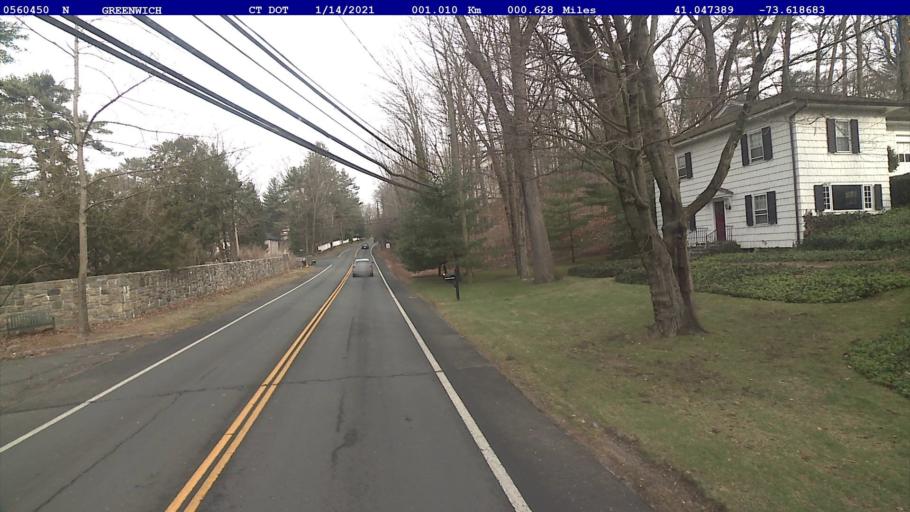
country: US
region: Connecticut
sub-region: Fairfield County
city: Greenwich
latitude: 41.0474
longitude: -73.6187
